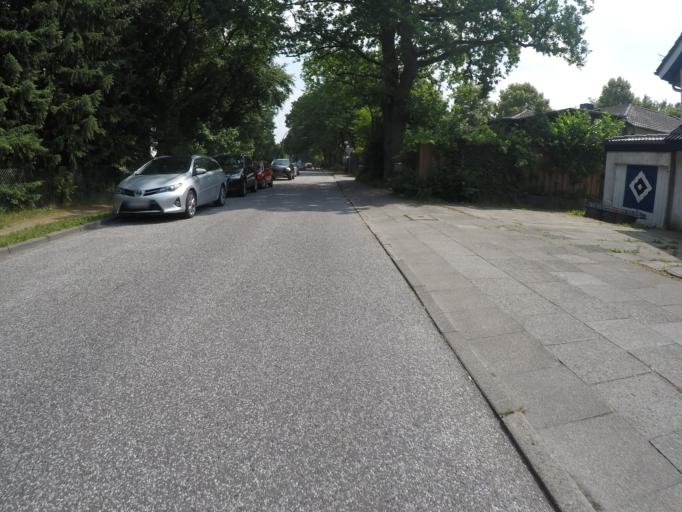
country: DE
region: Hamburg
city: Sasel
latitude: 53.6444
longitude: 10.1205
